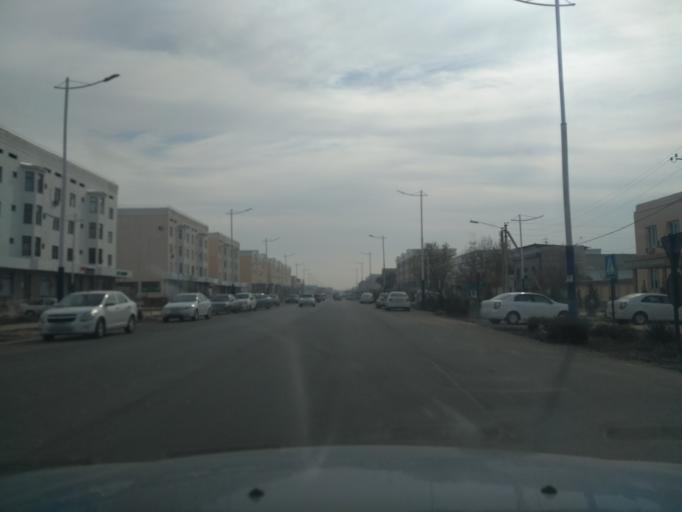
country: UZ
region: Sirdaryo
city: Guliston
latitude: 40.5080
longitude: 68.7698
